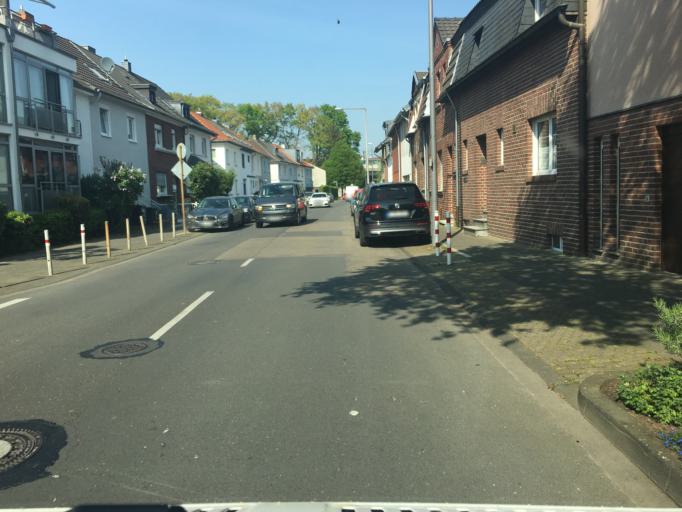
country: DE
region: North Rhine-Westphalia
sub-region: Regierungsbezirk Koln
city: Frechen
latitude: 50.9407
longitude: 6.8277
